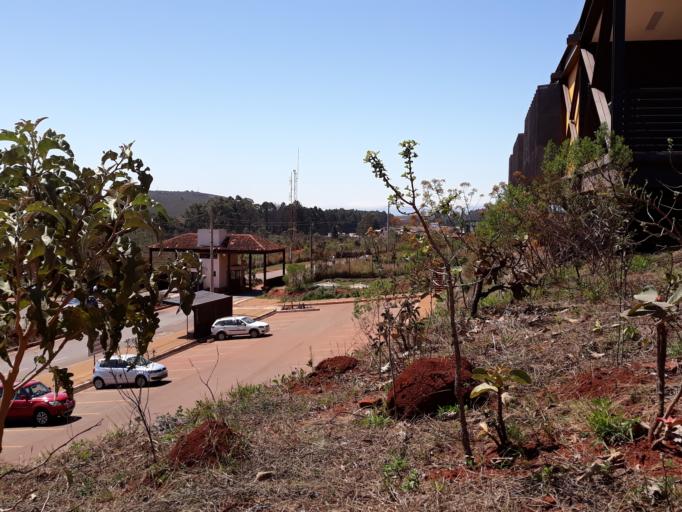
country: BR
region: Minas Gerais
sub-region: Ibirite
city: Ibirite
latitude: -20.0523
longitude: -44.0008
